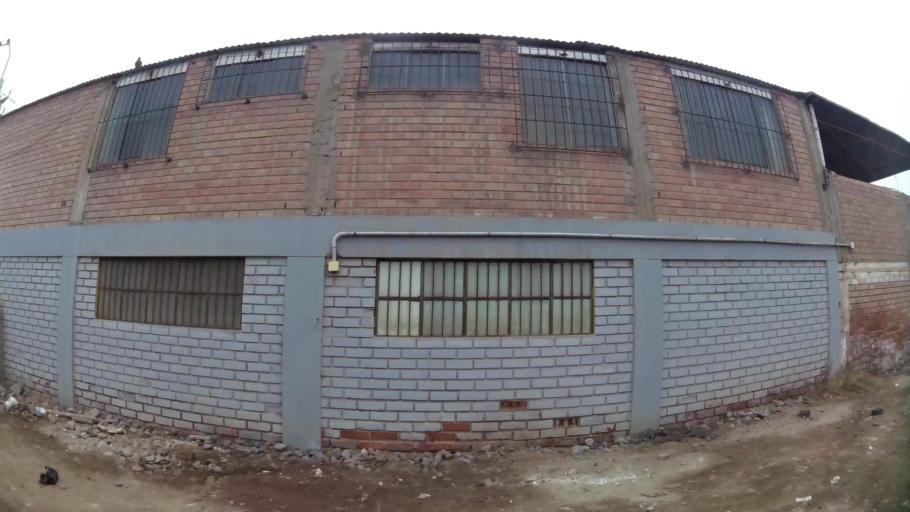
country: PE
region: Lima
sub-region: Lima
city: Surco
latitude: -12.2048
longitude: -77.0035
